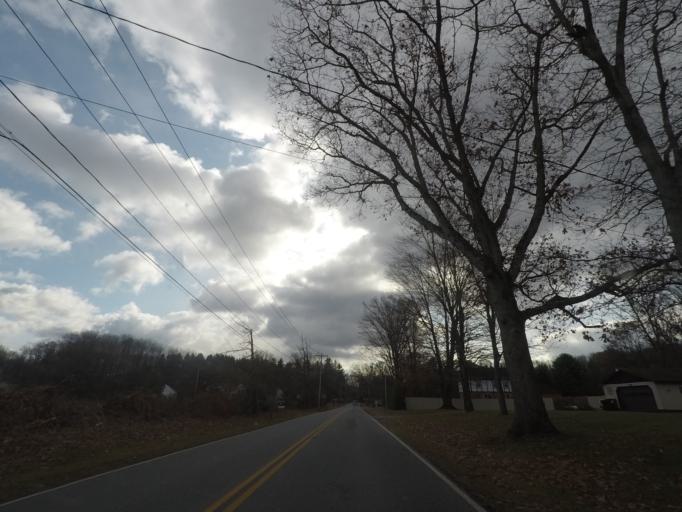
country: US
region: New York
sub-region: Saratoga County
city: Ballston Spa
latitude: 43.0069
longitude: -73.8086
